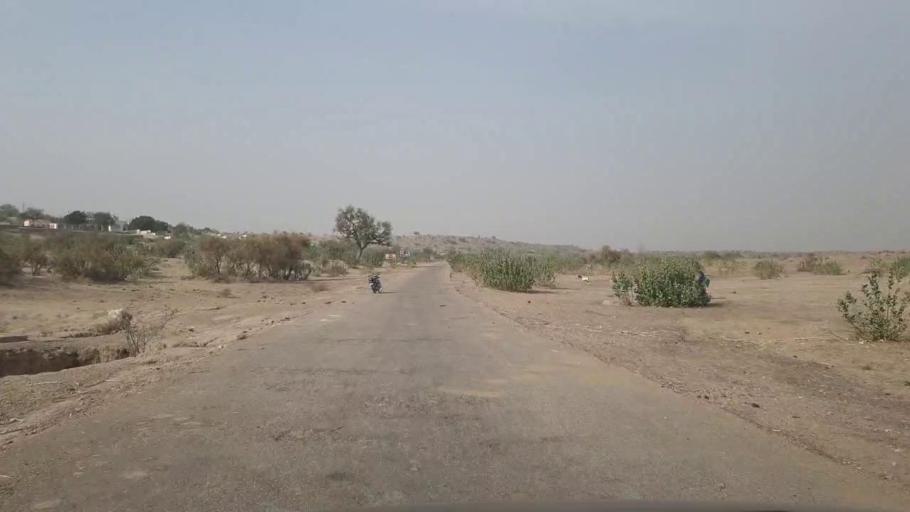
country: PK
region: Sindh
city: Chor
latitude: 25.6208
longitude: 69.9276
